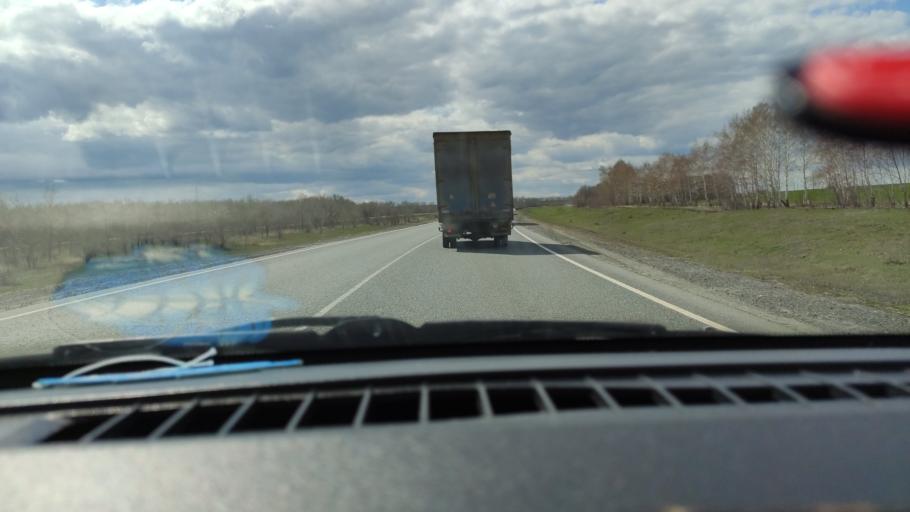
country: RU
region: Saratov
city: Balakovo
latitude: 52.1083
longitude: 47.7460
